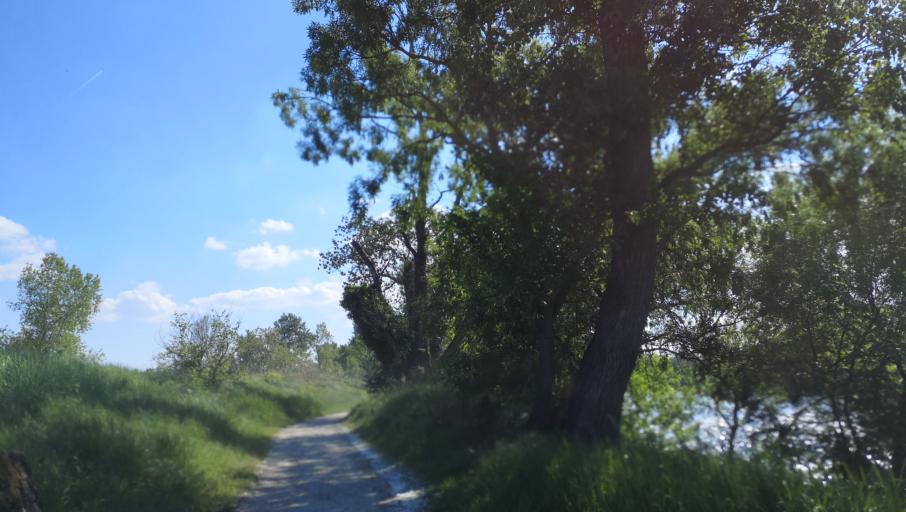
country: FR
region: Midi-Pyrenees
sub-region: Departement de la Haute-Garonne
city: Blagnac
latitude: 43.6518
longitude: 1.4052
